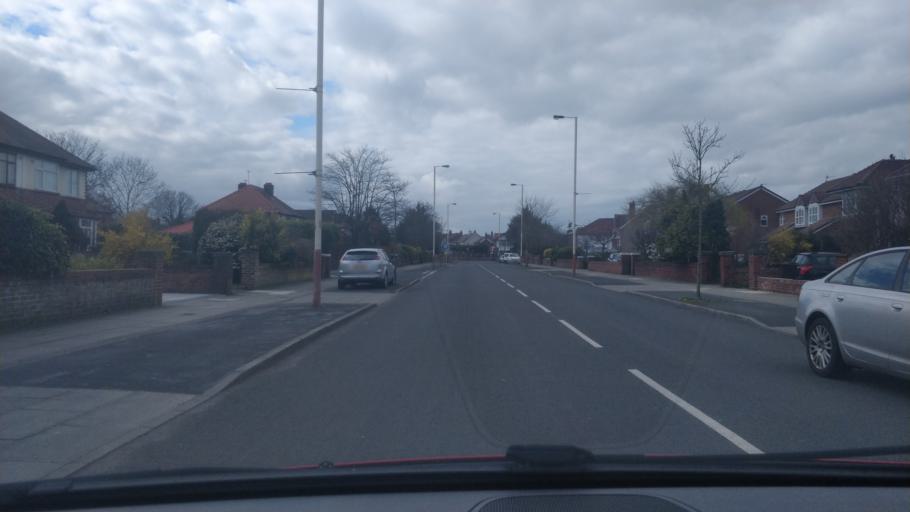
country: GB
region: England
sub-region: Sefton
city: Southport
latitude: 53.6121
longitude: -3.0179
